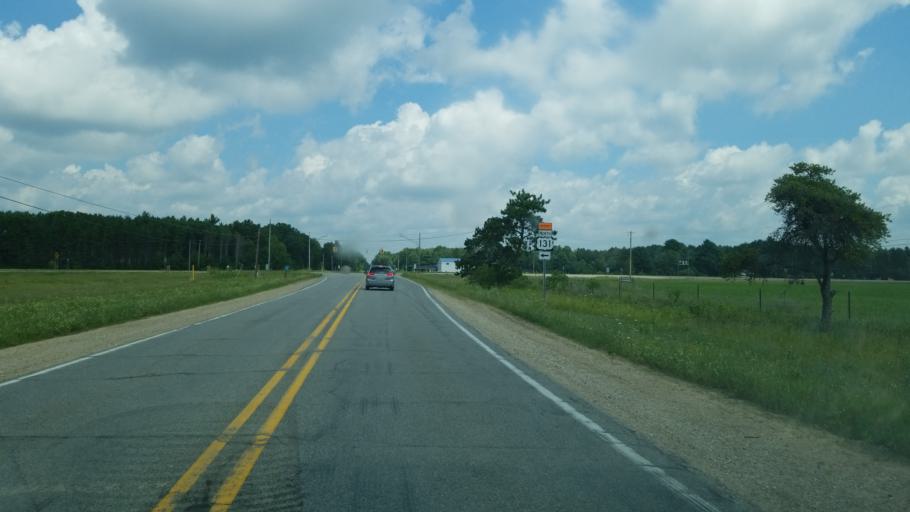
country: US
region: Michigan
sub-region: Montcalm County
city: Howard City
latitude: 43.4294
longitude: -85.4609
